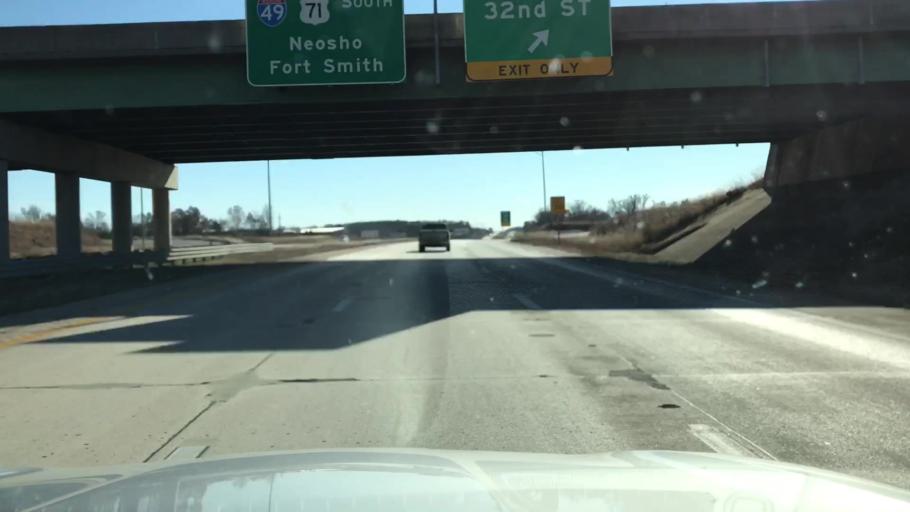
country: US
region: Missouri
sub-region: Jasper County
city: Duenweg
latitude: 37.0548
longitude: -94.4266
